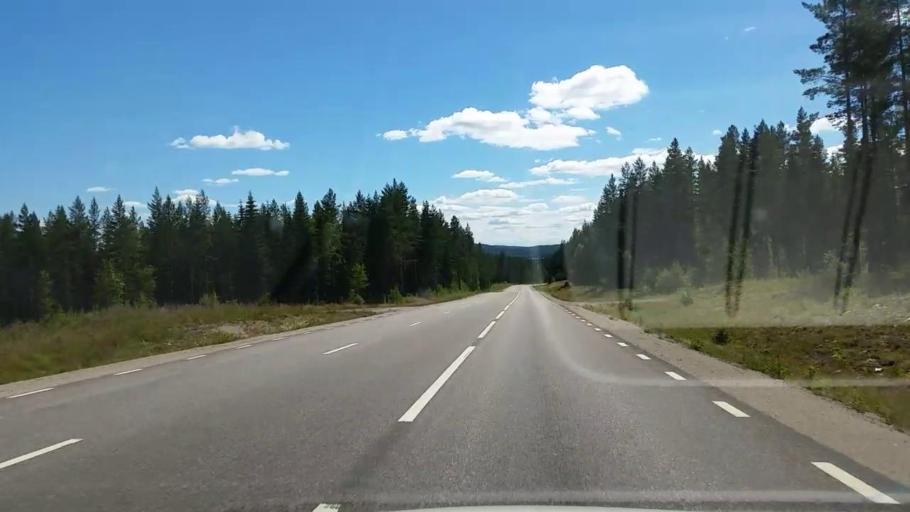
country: SE
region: Gaevleborg
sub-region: Bollnas Kommun
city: Vittsjo
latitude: 61.0546
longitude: 15.8022
